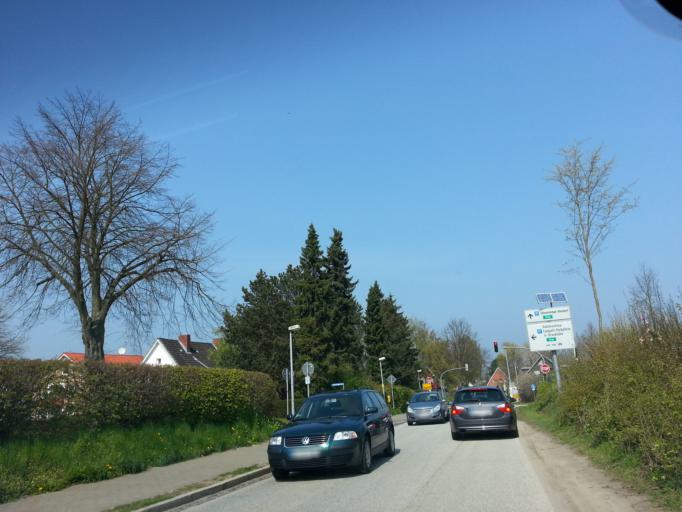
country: DE
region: Schleswig-Holstein
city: Travemuende
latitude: 53.9868
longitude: 10.8335
